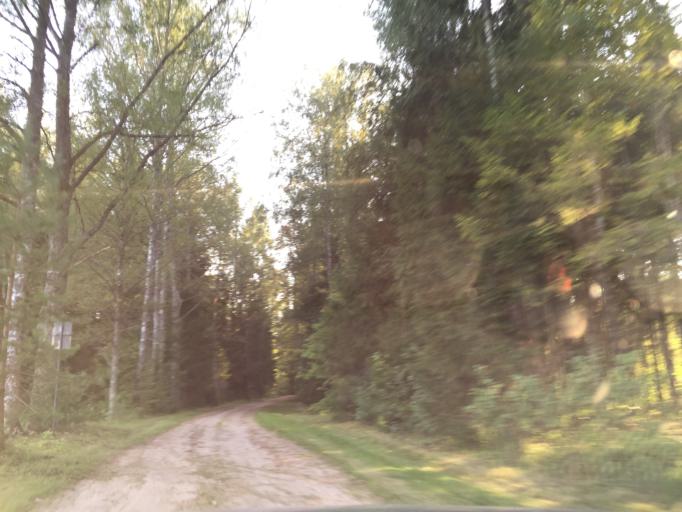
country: LV
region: Limbazu Rajons
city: Limbazi
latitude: 57.5578
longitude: 24.7839
